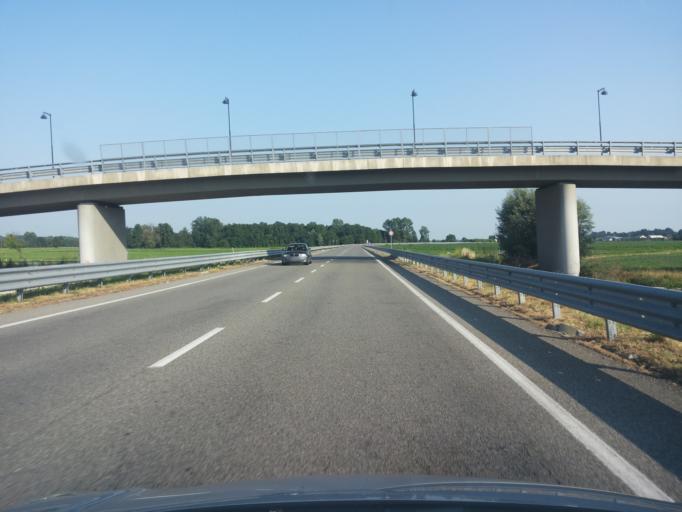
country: IT
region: Piedmont
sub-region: Provincia di Biella
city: Castelletto Cervo
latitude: 45.5185
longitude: 8.2073
